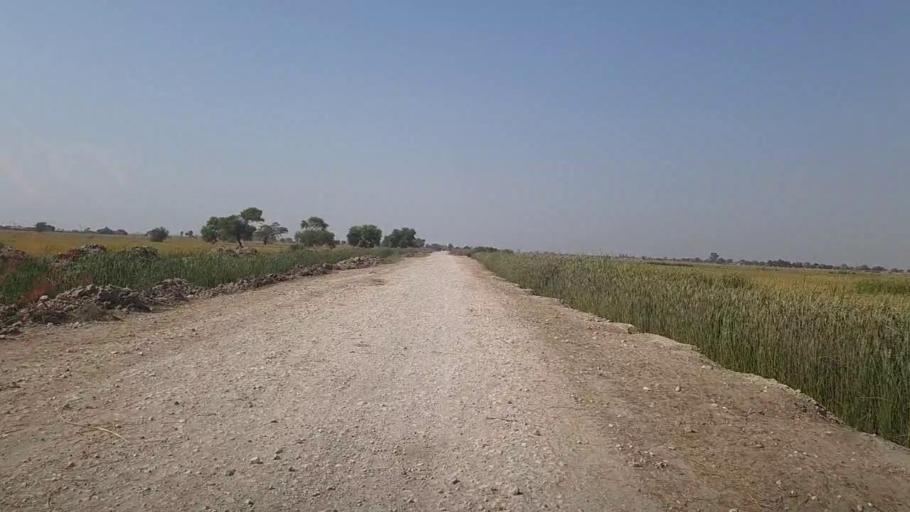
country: PK
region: Sindh
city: Kandhkot
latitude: 28.3967
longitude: 69.2711
